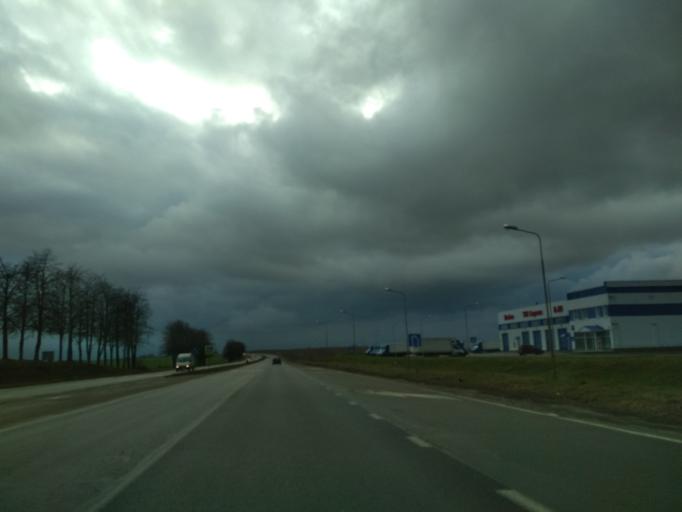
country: BY
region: Minsk
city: Luhavaya Slabada
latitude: 53.7579
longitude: 27.8302
